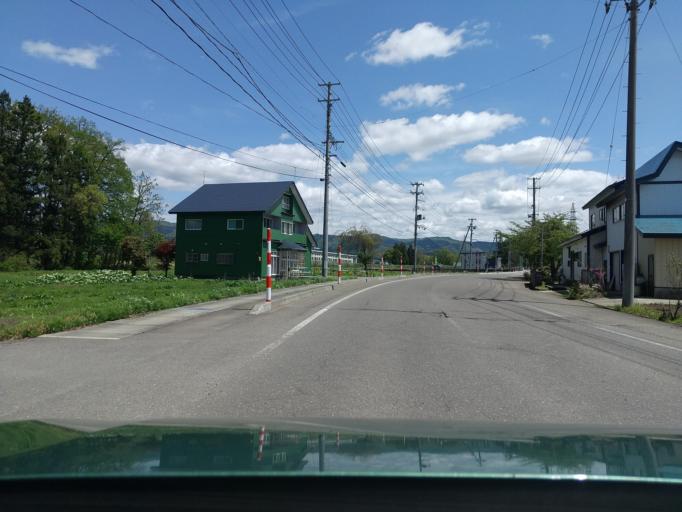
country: JP
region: Akita
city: Yokotemachi
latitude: 39.3534
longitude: 140.5450
